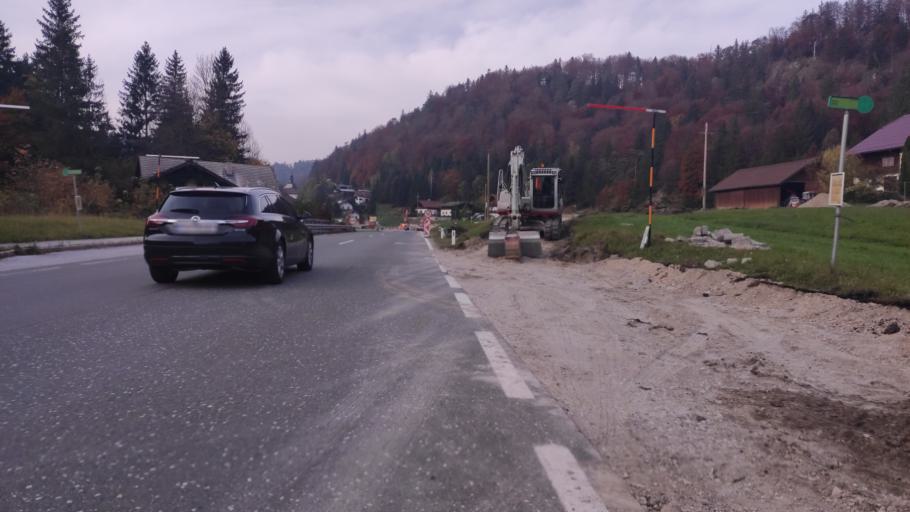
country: AT
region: Salzburg
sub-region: Politischer Bezirk Salzburg-Umgebung
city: Ebenau
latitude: 47.7856
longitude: 13.1785
